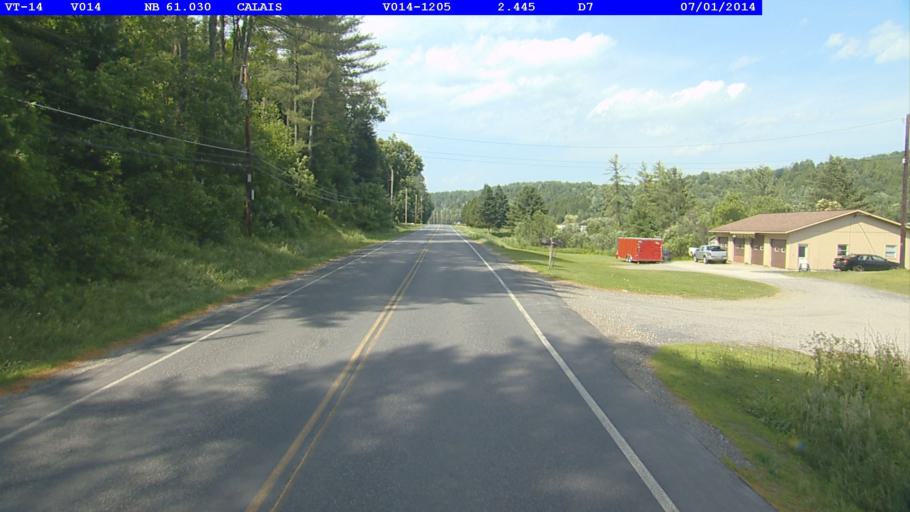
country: US
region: Vermont
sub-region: Washington County
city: Montpelier
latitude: 44.3415
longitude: -72.4432
